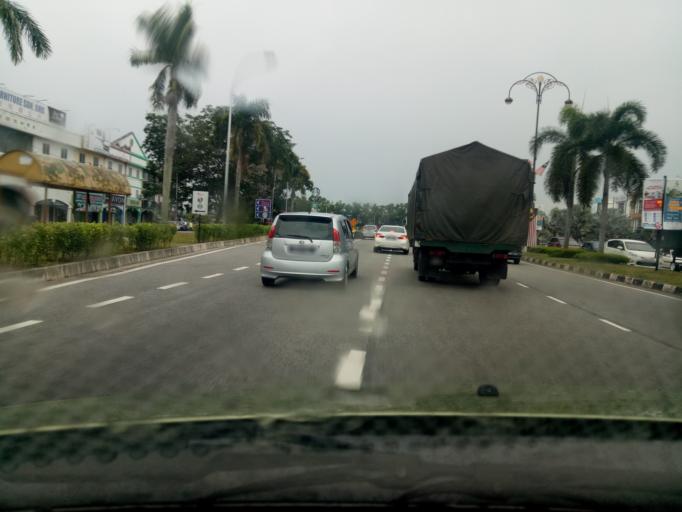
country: MY
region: Kedah
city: Sungai Petani
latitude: 5.6719
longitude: 100.5075
